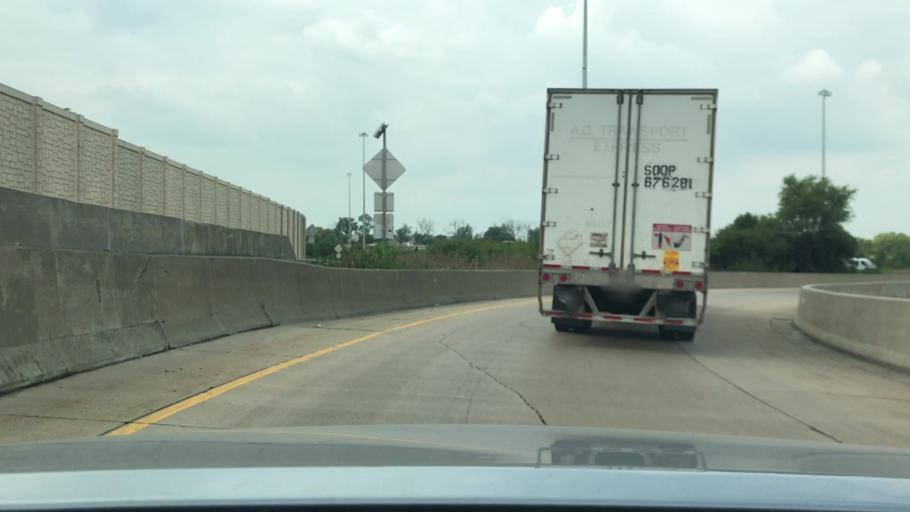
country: US
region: Illinois
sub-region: Cook County
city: Indian Head Park
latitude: 41.7589
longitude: -87.9032
